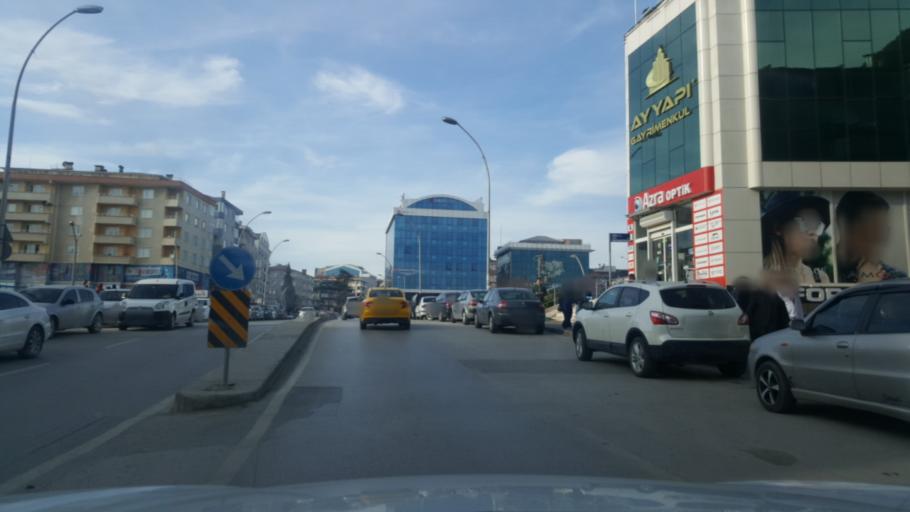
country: TR
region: Kocaeli
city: Gebze
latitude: 40.7939
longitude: 29.4334
